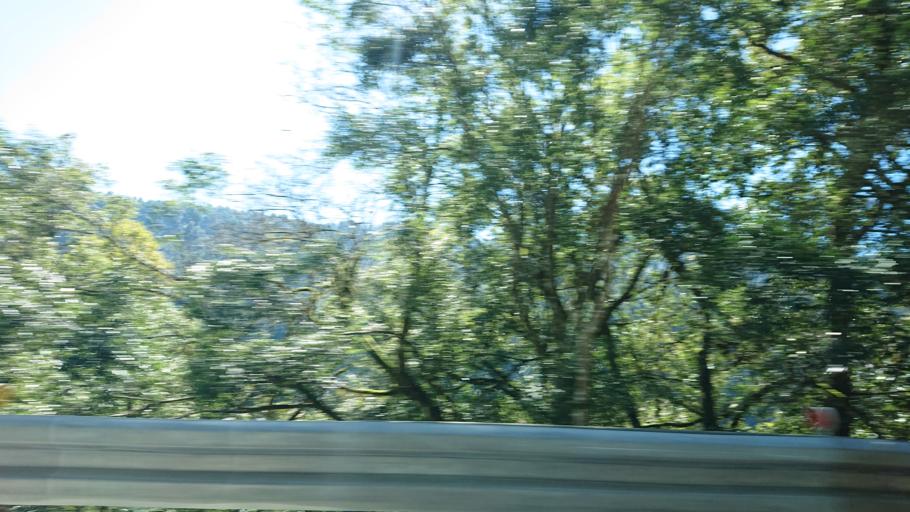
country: TW
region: Taiwan
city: Daxi
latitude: 24.4142
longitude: 121.3659
